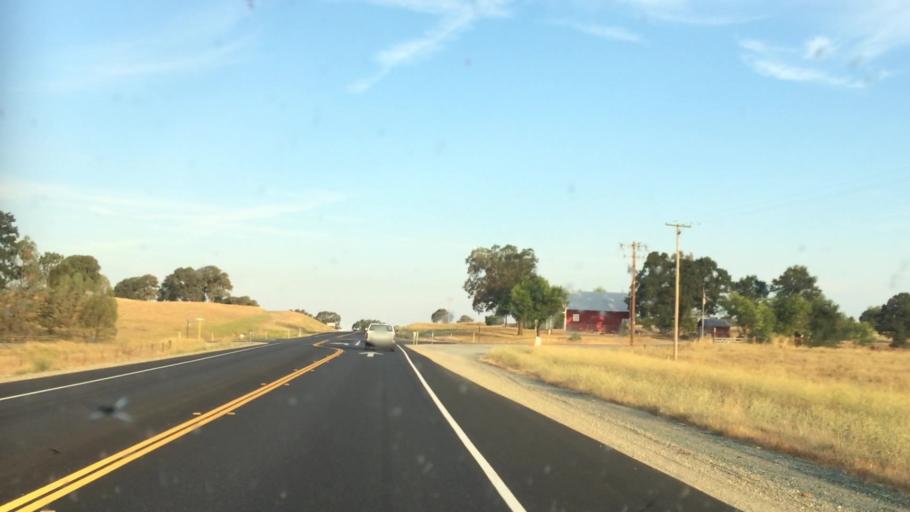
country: US
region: California
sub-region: Amador County
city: Plymouth
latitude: 38.4520
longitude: -120.9122
